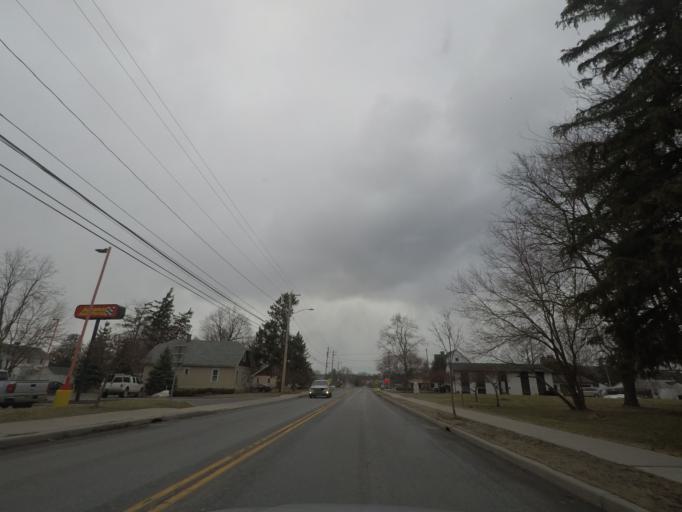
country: US
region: New York
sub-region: Madison County
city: Chittenango
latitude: 43.0512
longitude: -75.8659
